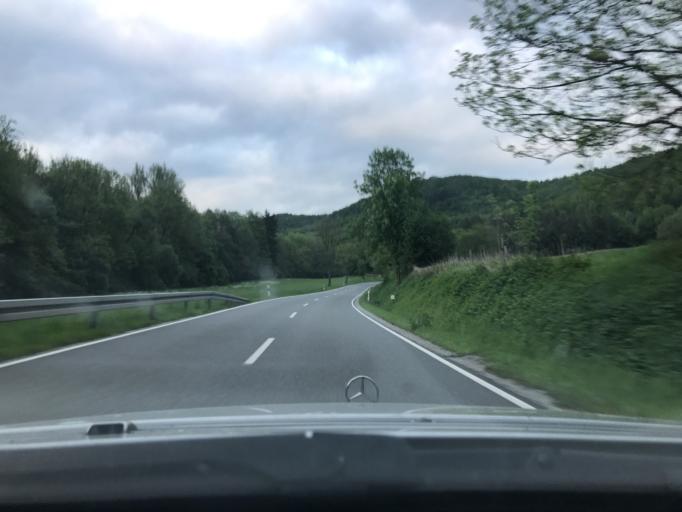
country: DE
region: Hesse
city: Wanfried
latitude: 51.1776
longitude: 10.2082
